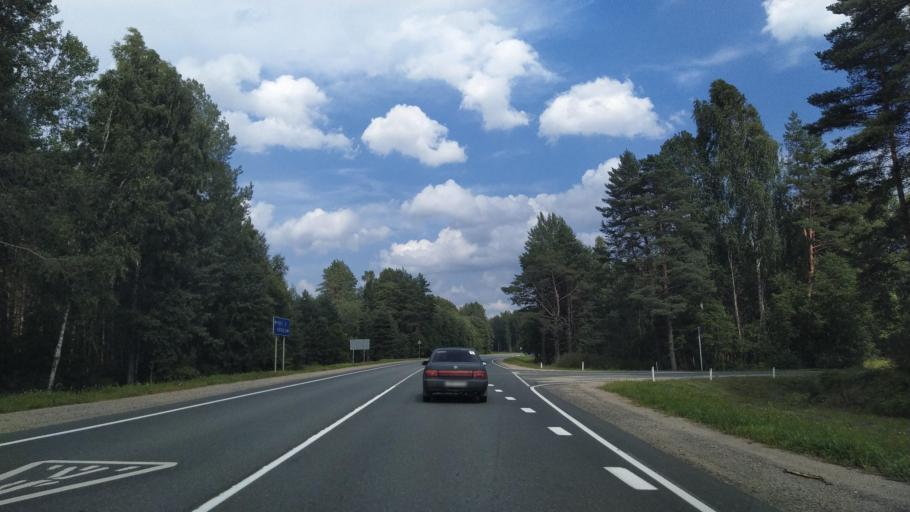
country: RU
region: Pskov
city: Porkhov
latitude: 57.8625
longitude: 29.5780
